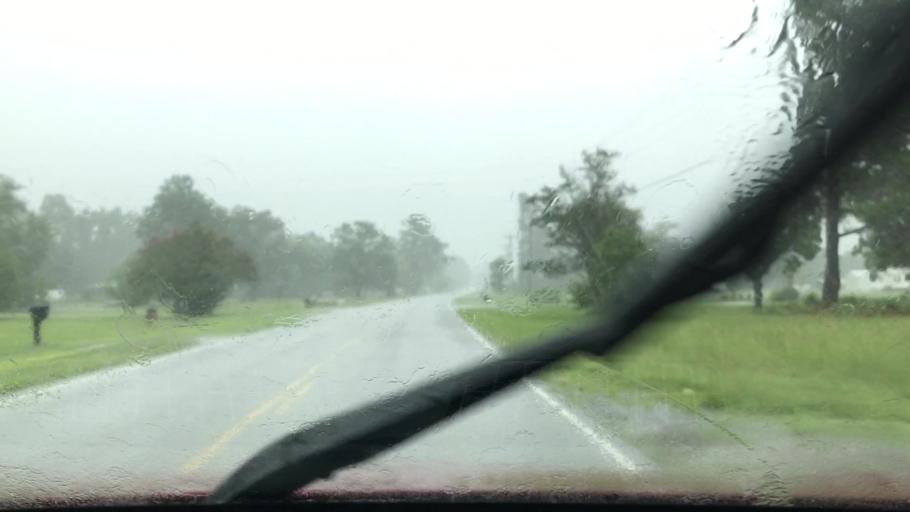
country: US
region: South Carolina
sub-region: Horry County
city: Red Hill
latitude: 33.8868
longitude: -78.9596
